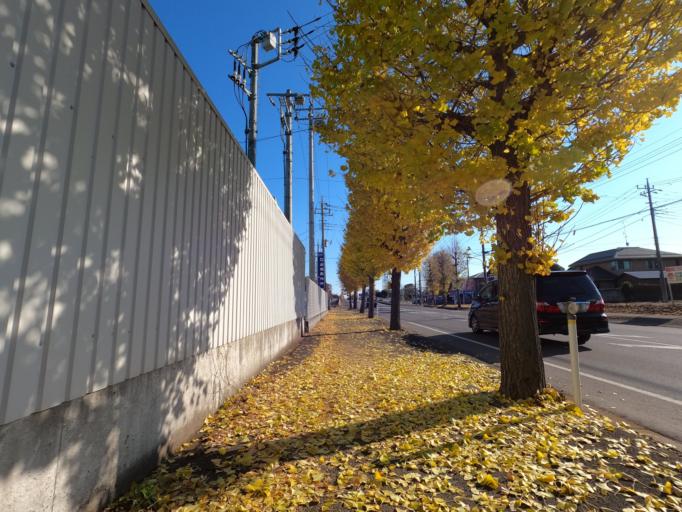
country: JP
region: Ibaraki
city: Moriya
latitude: 35.9598
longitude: 139.9756
